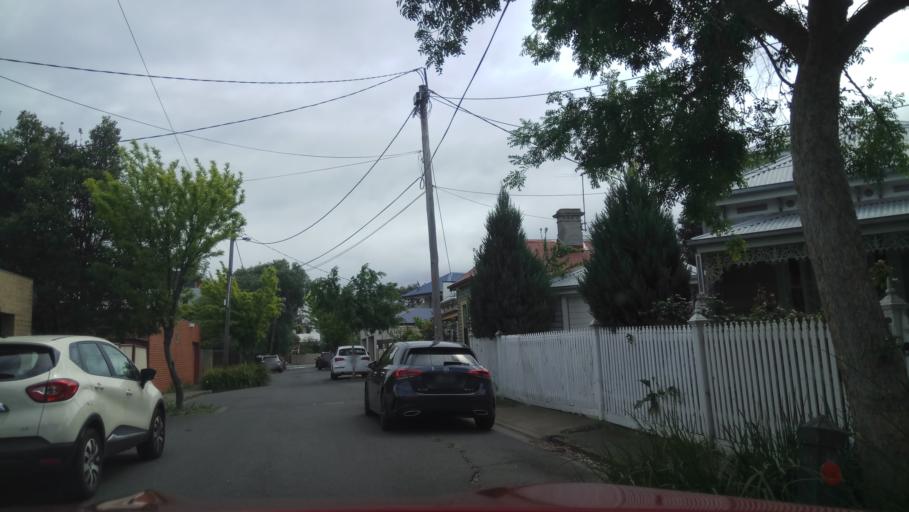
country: AU
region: Victoria
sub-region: Hobsons Bay
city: Williamstown
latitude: -37.8576
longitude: 144.8919
